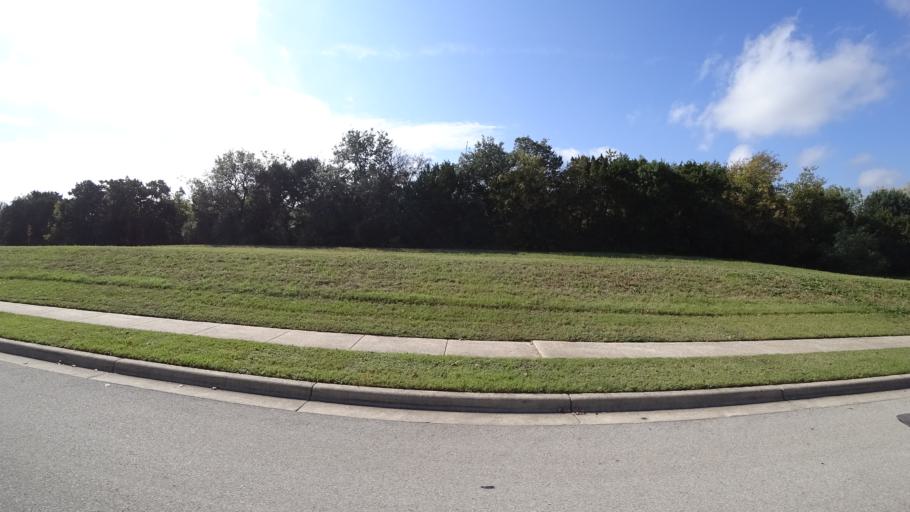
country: US
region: Texas
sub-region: Travis County
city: Shady Hollow
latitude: 30.1901
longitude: -97.8200
